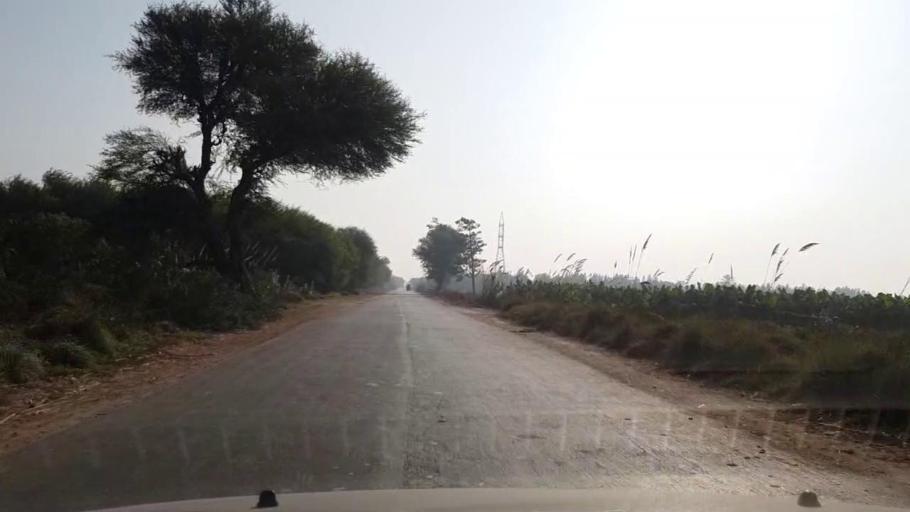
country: PK
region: Sindh
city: Matiari
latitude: 25.5961
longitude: 68.4637
